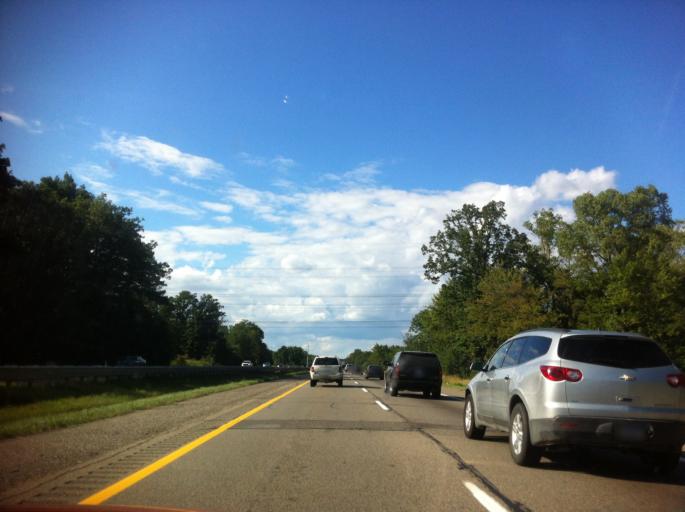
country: US
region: Michigan
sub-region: Washtenaw County
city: Ann Arbor
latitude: 42.3490
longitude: -83.7465
